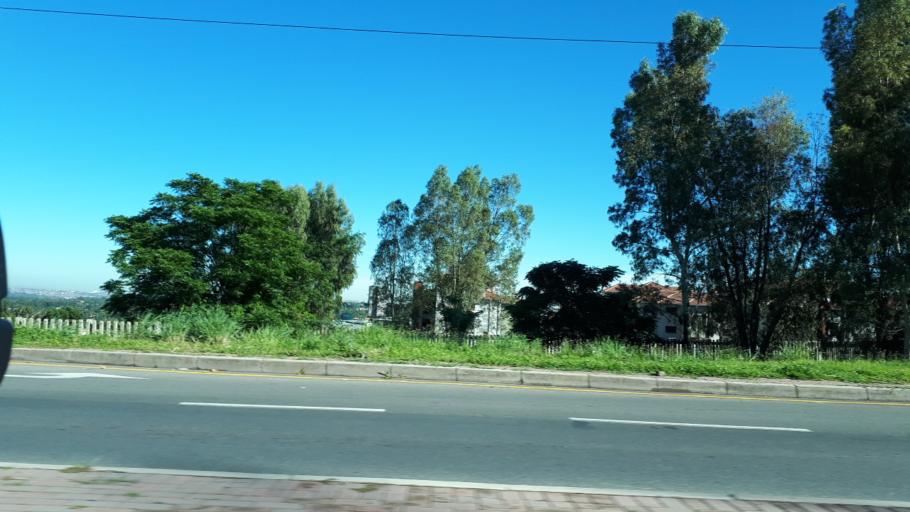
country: ZA
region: Gauteng
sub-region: Ekurhuleni Metropolitan Municipality
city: Germiston
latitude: -26.1732
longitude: 28.1612
